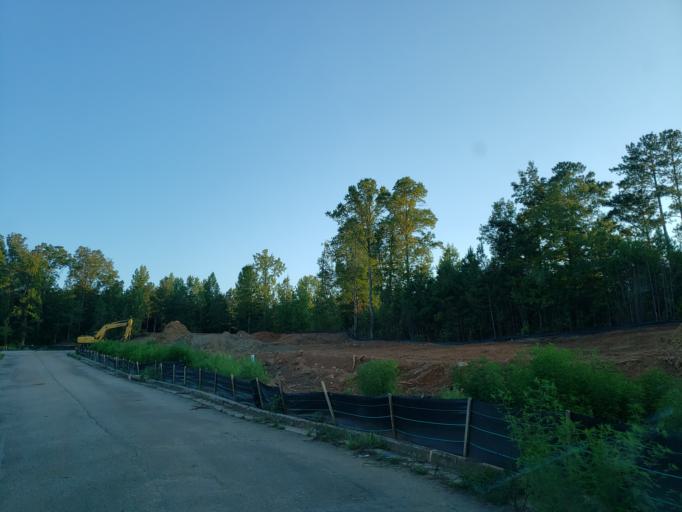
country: US
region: Georgia
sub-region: Paulding County
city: Dallas
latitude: 33.9970
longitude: -84.7715
